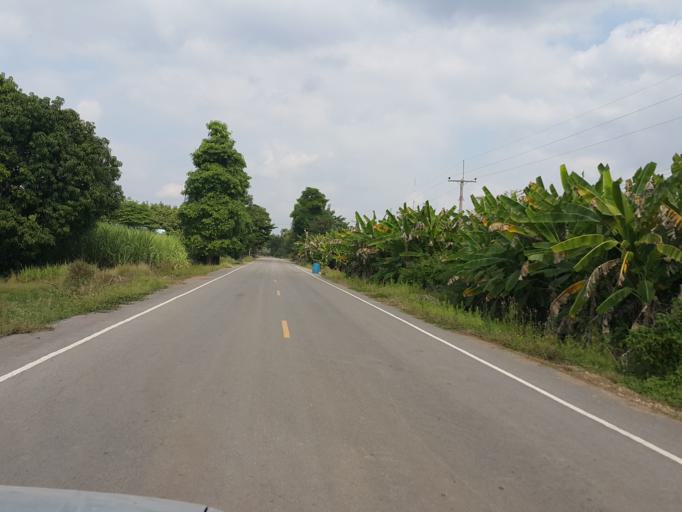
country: TH
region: Sukhothai
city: Thung Saliam
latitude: 17.4127
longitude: 99.5785
